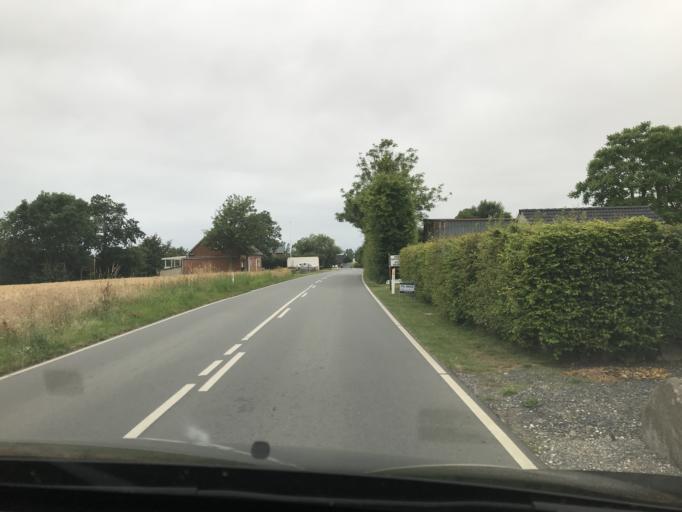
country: DK
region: South Denmark
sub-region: AEro Kommune
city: AEroskobing
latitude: 54.8624
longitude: 10.3771
